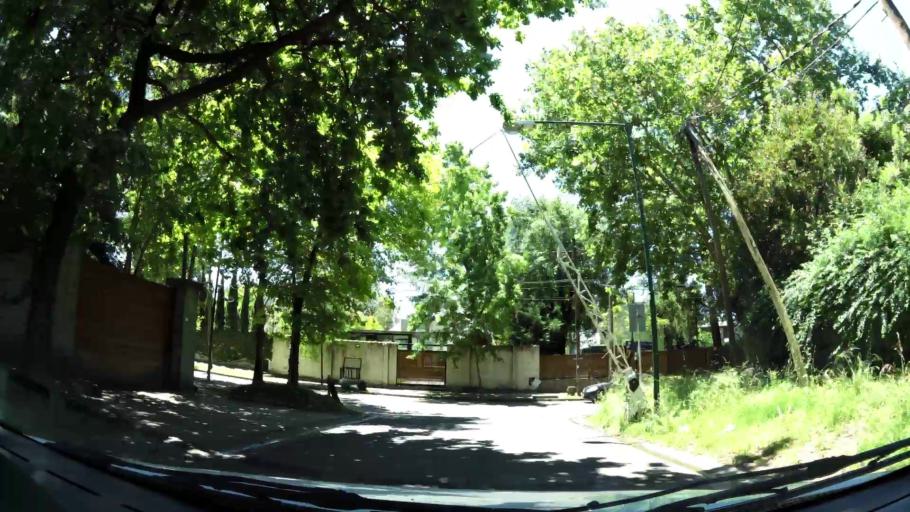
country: AR
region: Buenos Aires
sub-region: Partido de San Isidro
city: San Isidro
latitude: -34.4963
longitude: -58.5615
